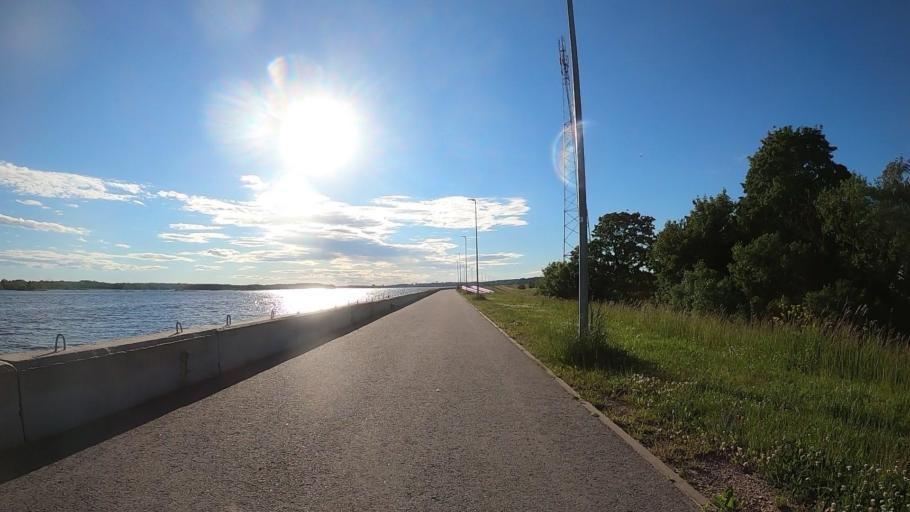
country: LV
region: Ikskile
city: Ikskile
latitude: 56.8299
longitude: 24.4829
